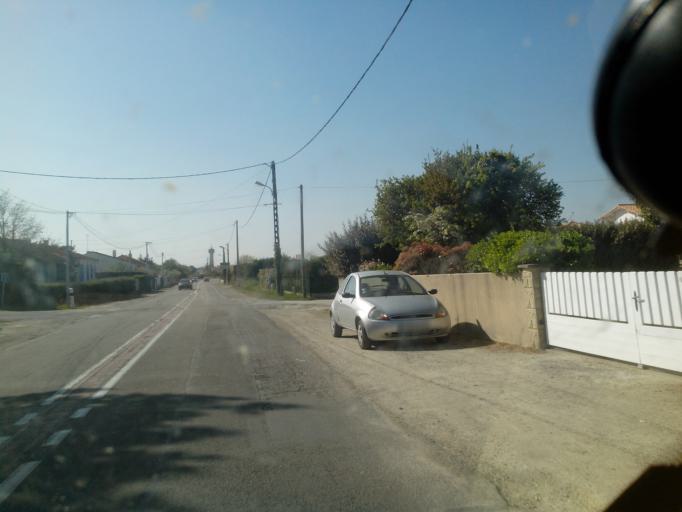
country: FR
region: Pays de la Loire
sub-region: Departement de la Loire-Atlantique
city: Pornic
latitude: 47.1050
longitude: -2.0686
